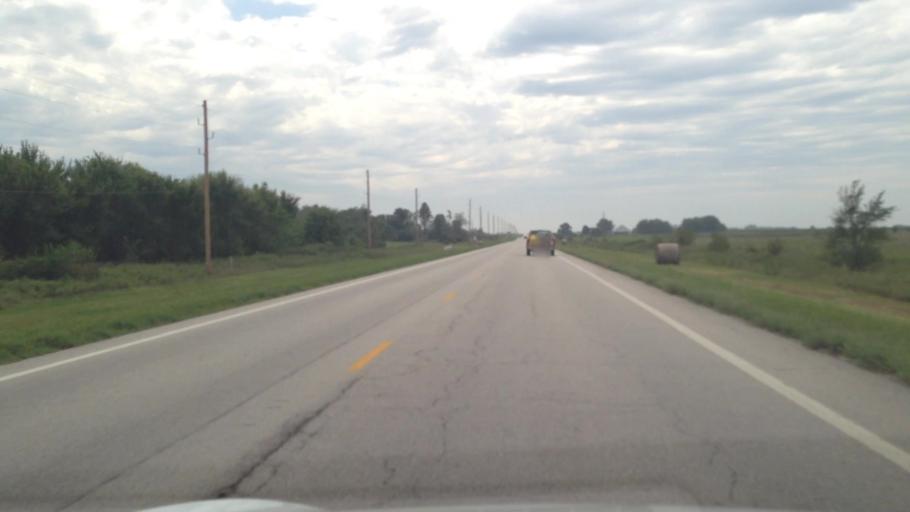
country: US
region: Kansas
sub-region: Allen County
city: Iola
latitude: 37.9490
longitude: -95.1700
